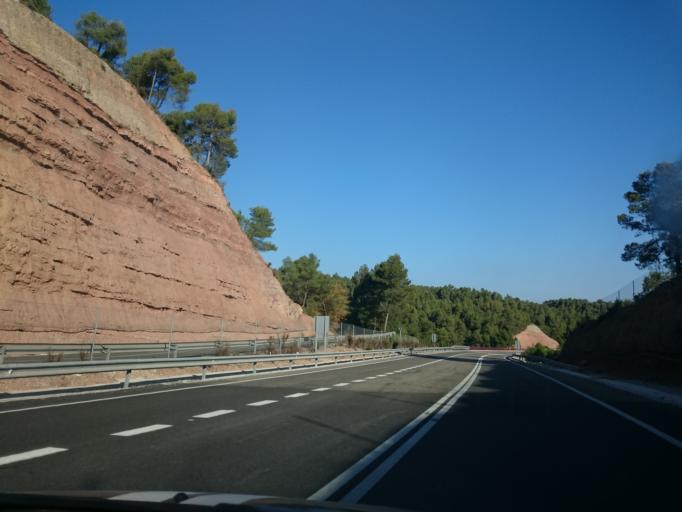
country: ES
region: Catalonia
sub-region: Provincia de Barcelona
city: Castellfollit del Boix
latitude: 41.6426
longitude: 1.7031
